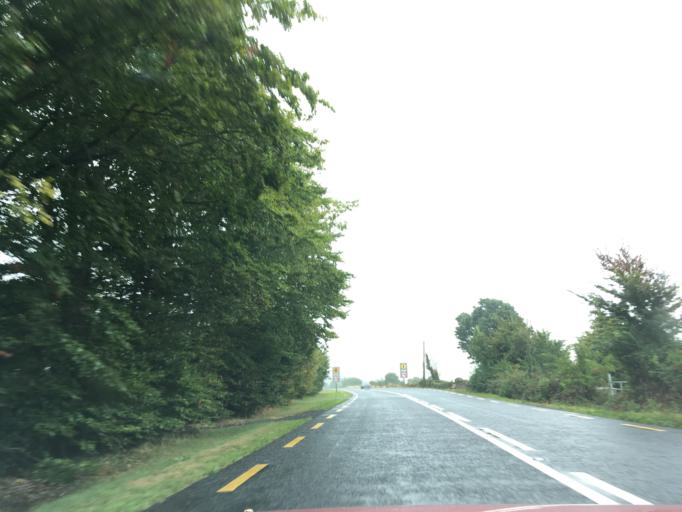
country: IE
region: Munster
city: Carrick-on-Suir
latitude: 52.3519
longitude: -7.4659
